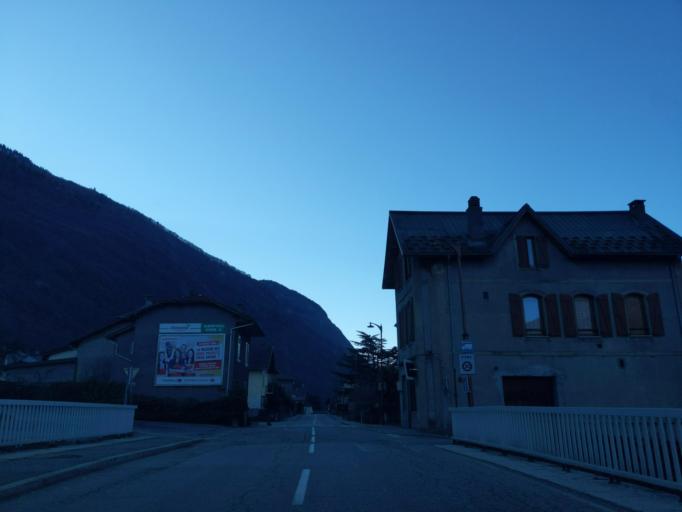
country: FR
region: Rhone-Alpes
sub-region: Departement de la Savoie
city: La Bathie
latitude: 45.6177
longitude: 6.4512
